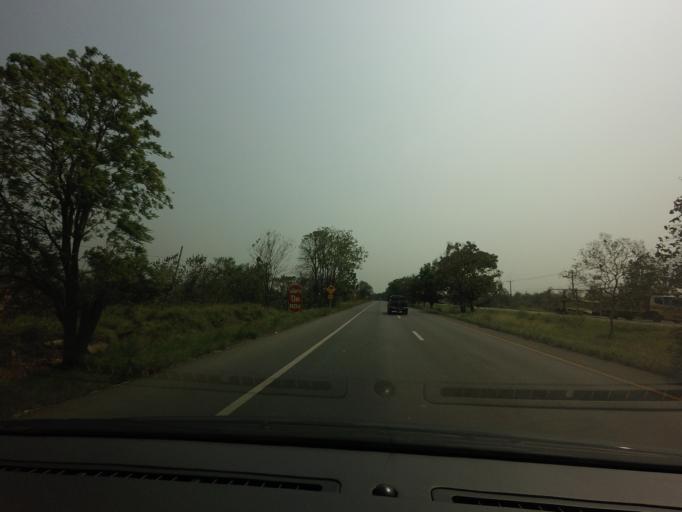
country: TH
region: Prachuap Khiri Khan
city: Pran Buri
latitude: 12.4642
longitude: 99.8973
